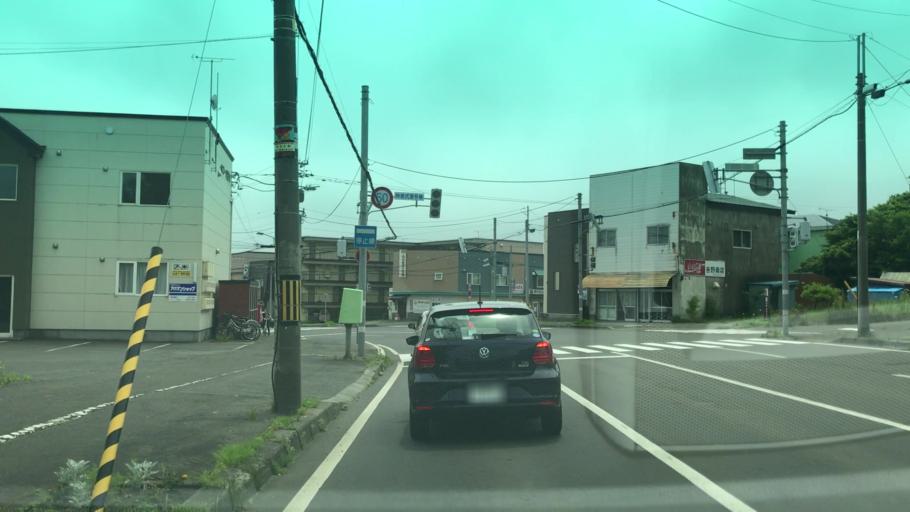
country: JP
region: Hokkaido
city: Muroran
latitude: 42.3658
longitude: 141.0365
